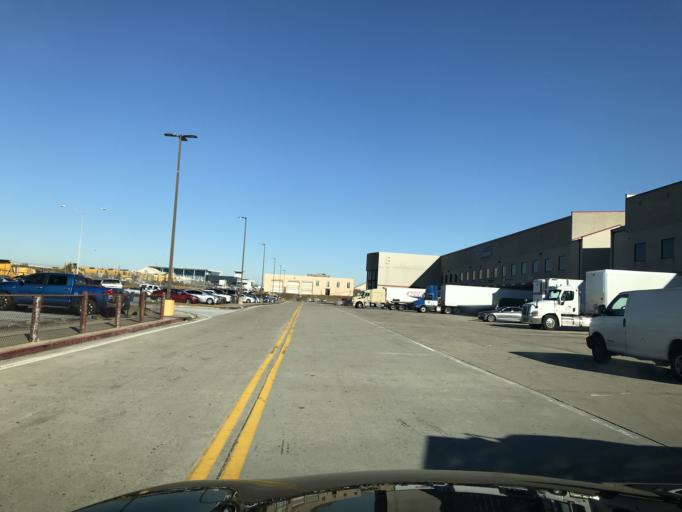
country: US
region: Georgia
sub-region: Fulton County
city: College Park
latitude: 33.6265
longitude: -84.4310
